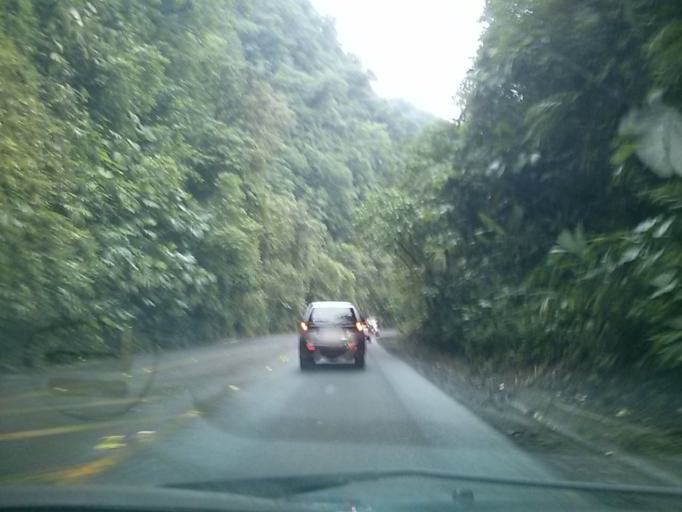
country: CR
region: San Jose
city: Dulce Nombre de Jesus
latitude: 10.1000
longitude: -83.9774
